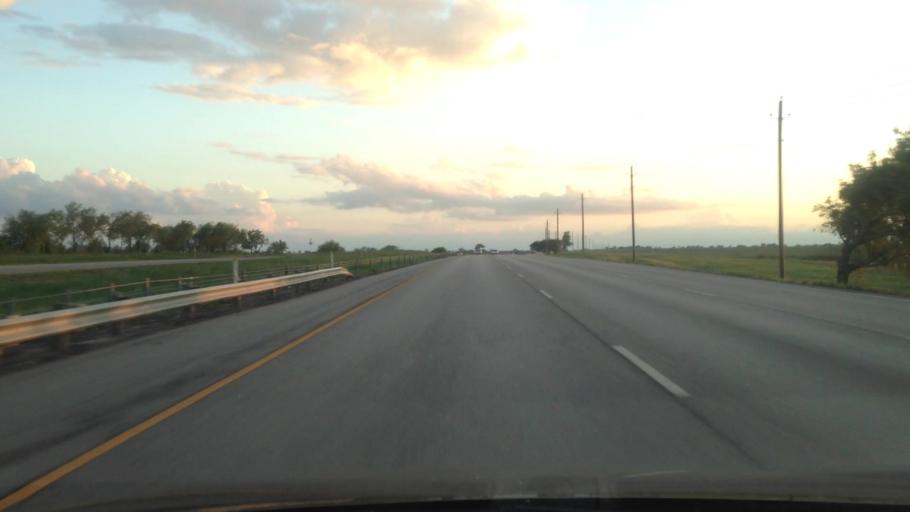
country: US
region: Texas
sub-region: Tarrant County
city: Benbrook
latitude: 32.6497
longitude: -97.5010
